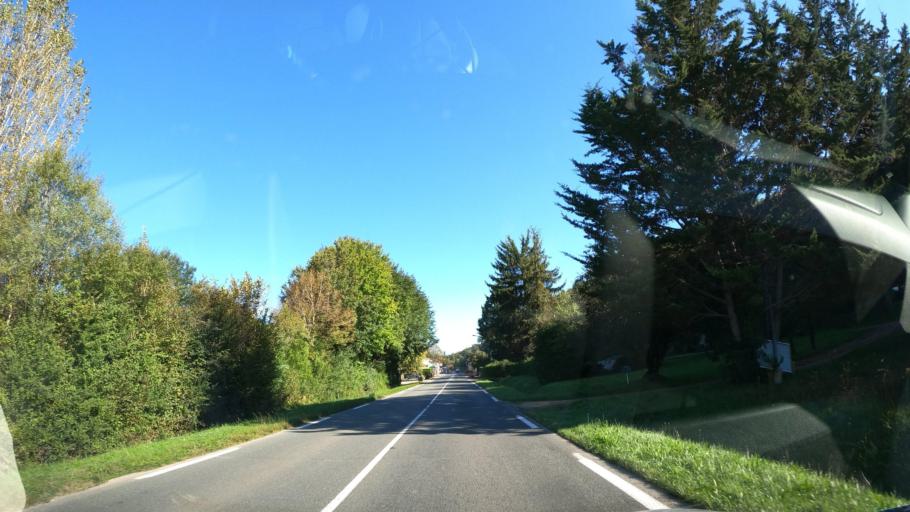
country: FR
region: Aquitaine
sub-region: Departement de la Dordogne
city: Lembras
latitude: 44.9330
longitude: 0.5617
